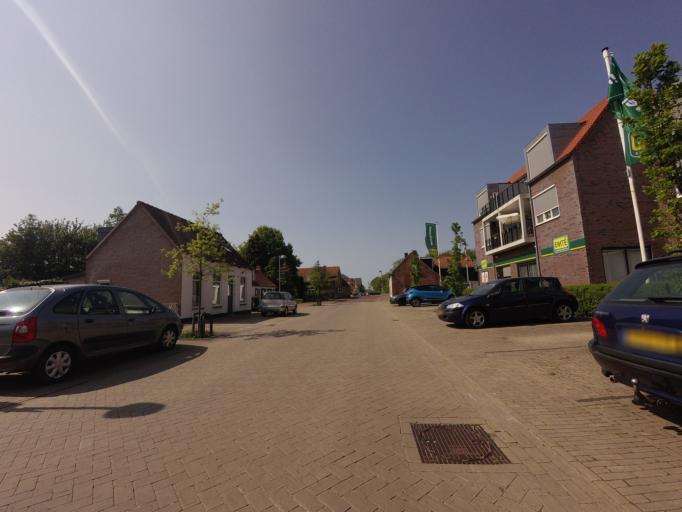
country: NL
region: Zeeland
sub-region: Gemeente Middelburg
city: Middelburg
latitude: 51.5482
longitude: 3.5922
